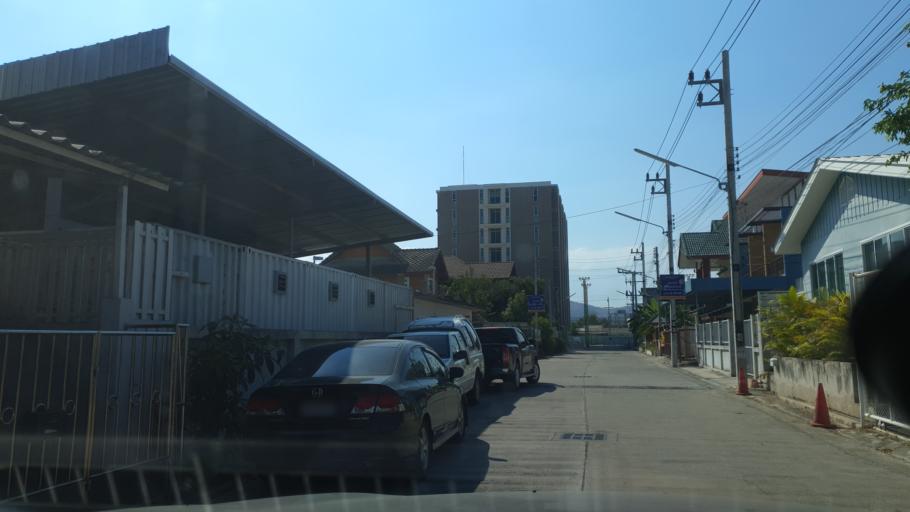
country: TH
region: Prachuap Khiri Khan
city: Hua Hin
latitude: 12.5544
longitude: 99.9599
